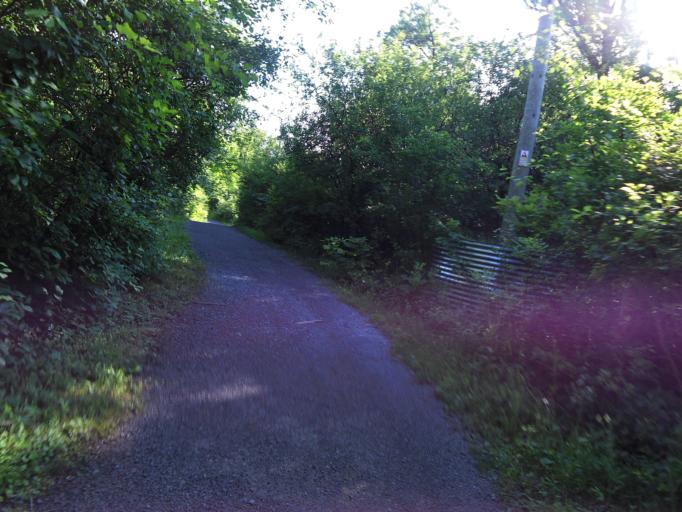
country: CA
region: Ontario
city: Bells Corners
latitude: 45.3502
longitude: -75.8569
